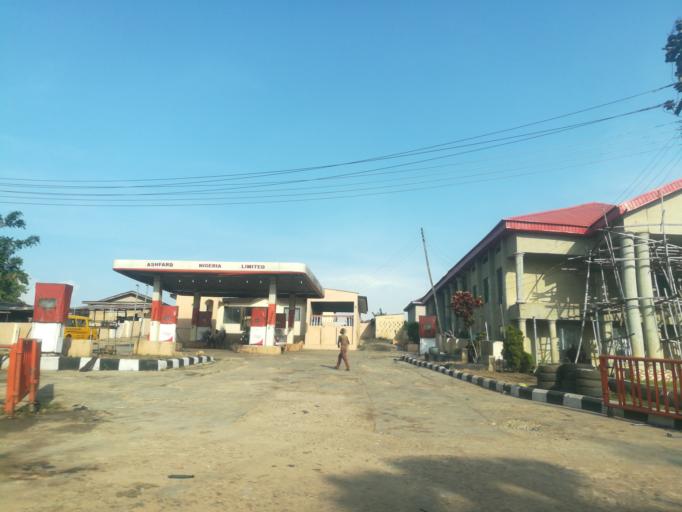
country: NG
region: Oyo
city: Moniya
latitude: 7.5226
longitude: 3.9120
